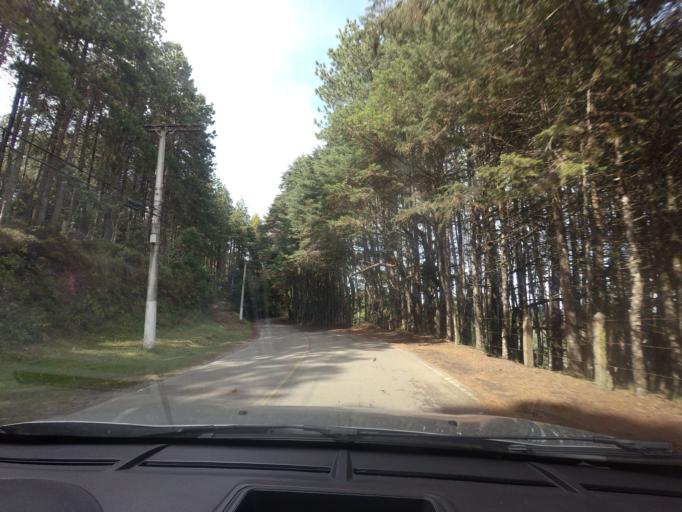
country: BR
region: Sao Paulo
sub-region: Campos Do Jordao
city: Campos do Jordao
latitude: -22.7649
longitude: -45.5991
